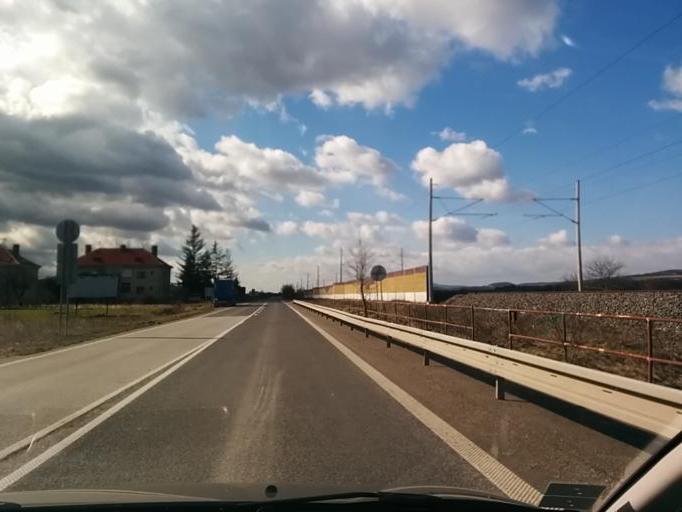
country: SK
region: Trenciansky
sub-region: Okres Trencin
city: Trencin
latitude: 48.8720
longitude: 17.9693
